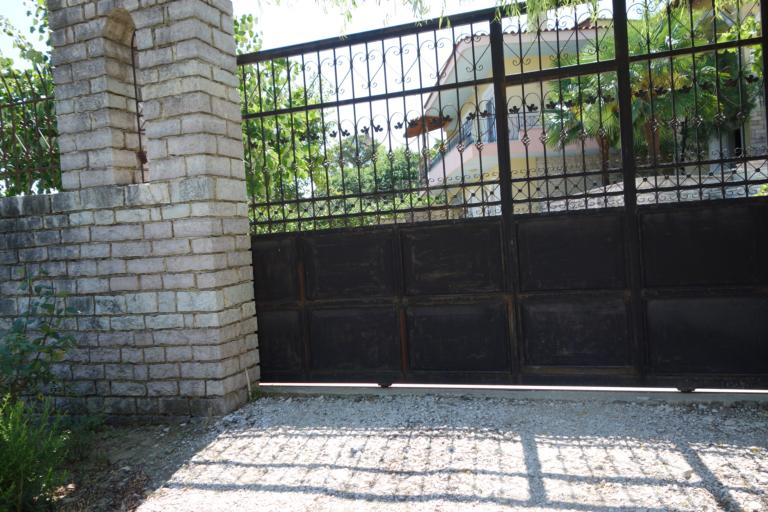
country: AL
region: Gjirokaster
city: Gjirokaster
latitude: 40.0826
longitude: 20.1321
